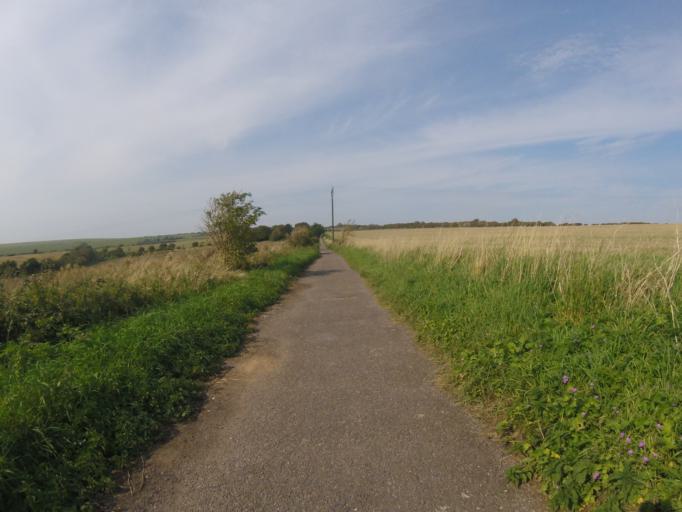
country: GB
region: England
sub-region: East Sussex
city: Portslade
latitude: 50.8703
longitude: -0.1990
